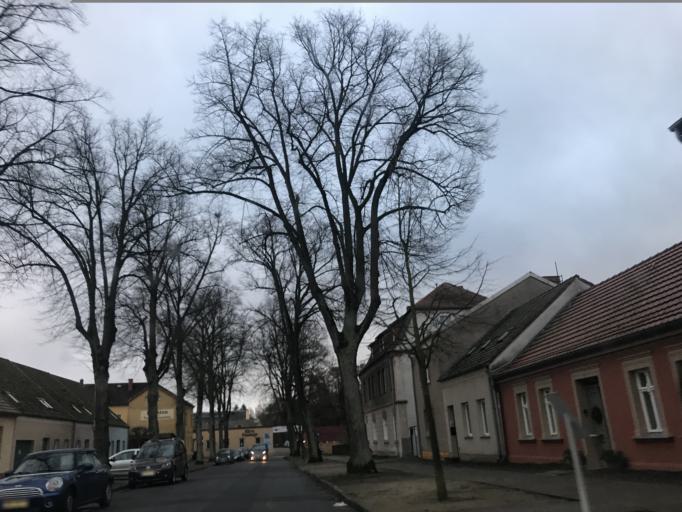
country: DE
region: Brandenburg
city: Rheinsberg
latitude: 53.0981
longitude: 12.8941
